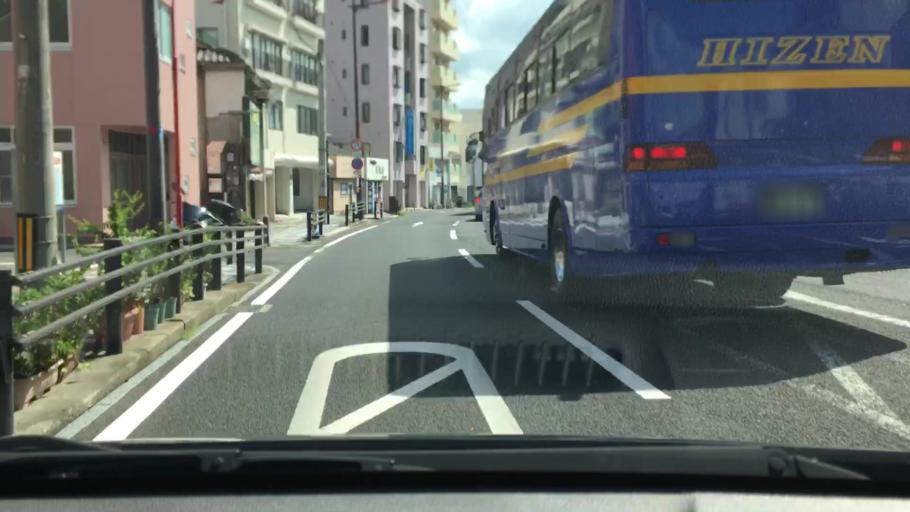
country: JP
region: Nagasaki
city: Sasebo
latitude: 33.1847
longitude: 129.7183
